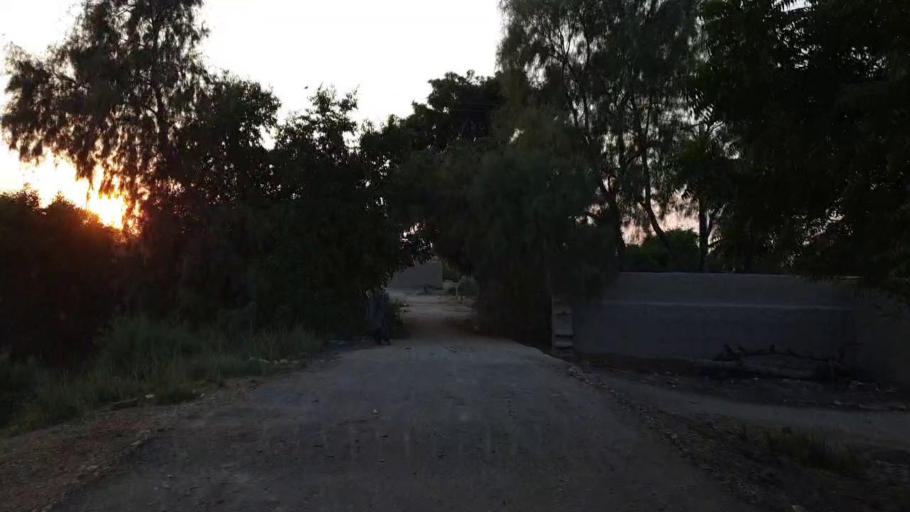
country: PK
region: Sindh
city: Sehwan
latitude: 26.4504
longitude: 67.7668
